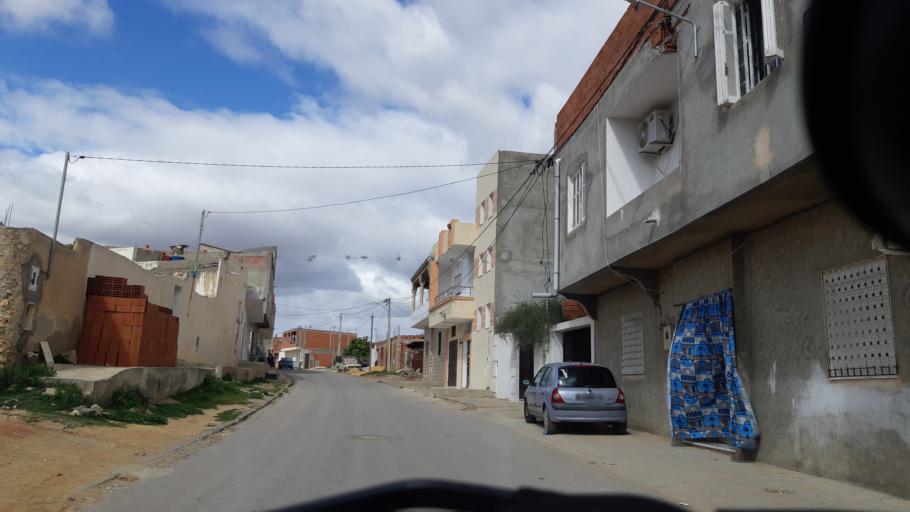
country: TN
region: Susah
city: Akouda
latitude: 35.8679
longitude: 10.5215
